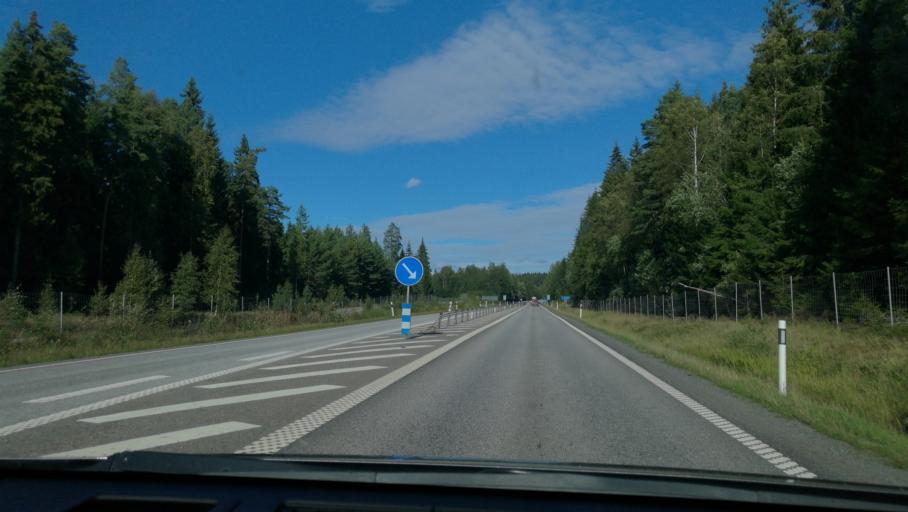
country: SE
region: Vaestra Goetaland
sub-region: Gullspangs Kommun
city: Anderstorp
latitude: 58.9364
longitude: 14.4303
